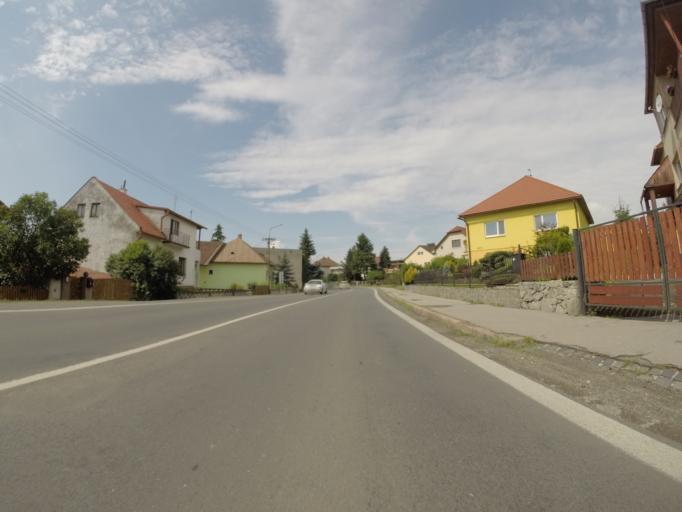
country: SK
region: Banskobystricky
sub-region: Okres Banska Bystrica
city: Zvolen
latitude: 48.6158
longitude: 19.1351
